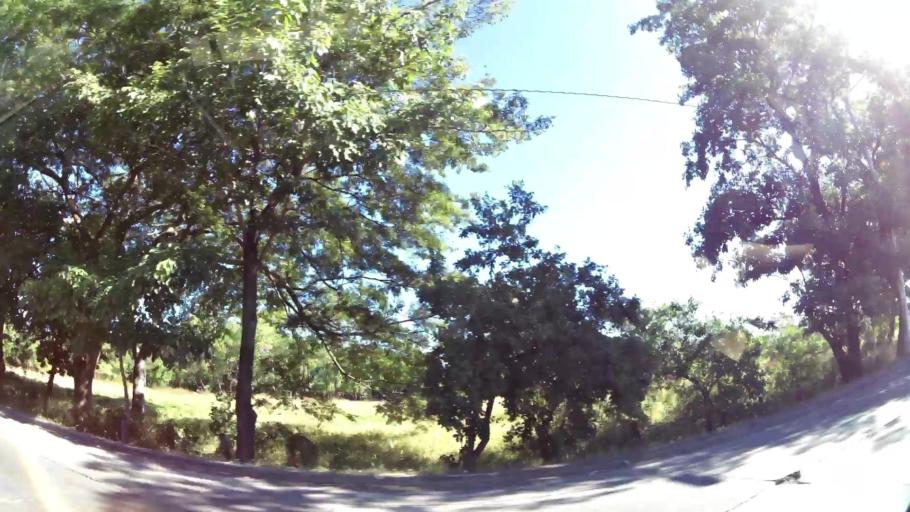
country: SV
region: San Miguel
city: San Miguel
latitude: 13.4586
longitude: -88.1464
